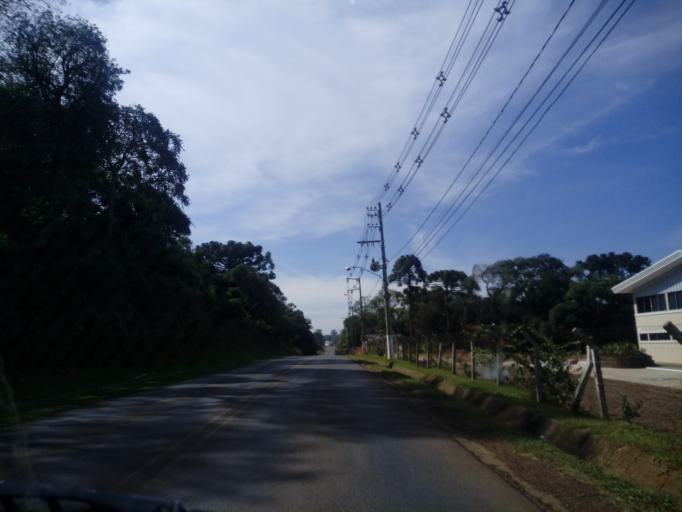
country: BR
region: Santa Catarina
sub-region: Chapeco
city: Chapeco
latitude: -27.0891
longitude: -52.6632
